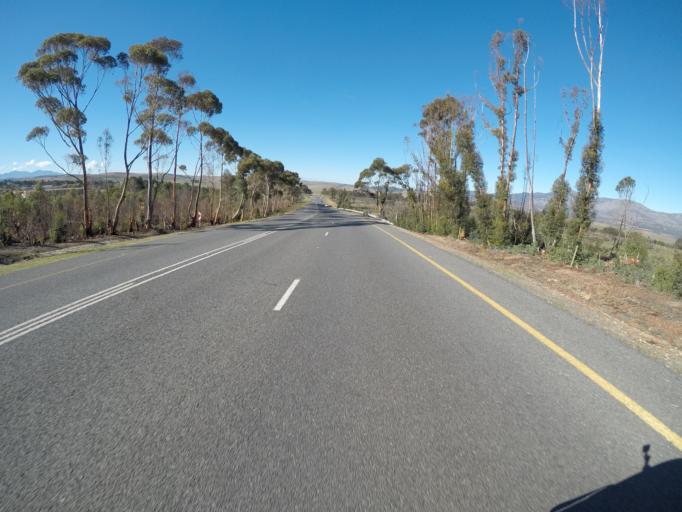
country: ZA
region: Western Cape
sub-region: Overberg District Municipality
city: Hermanus
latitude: -34.2350
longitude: 19.1938
